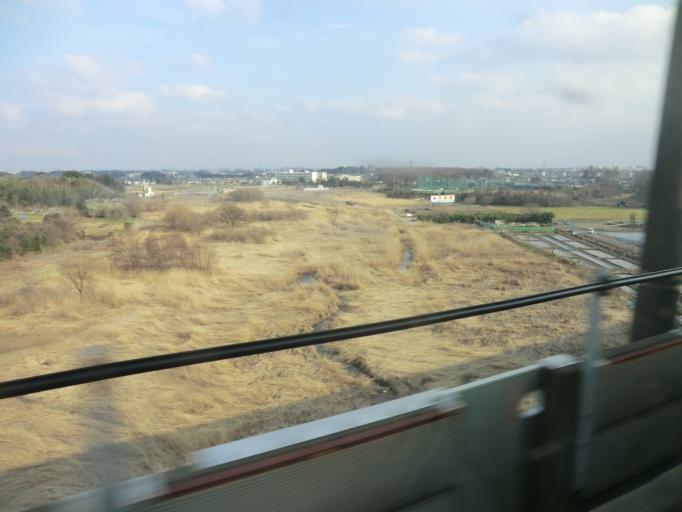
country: JP
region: Saitama
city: Ageoshimo
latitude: 35.9754
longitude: 139.6247
